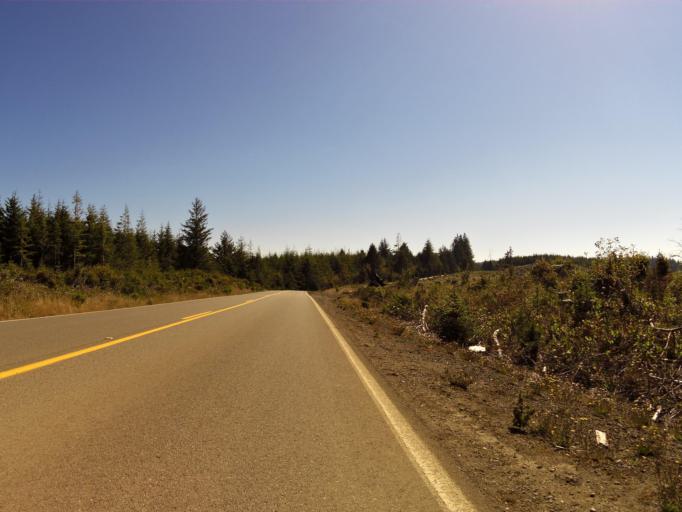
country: US
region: Oregon
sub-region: Coos County
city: Barview
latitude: 43.2568
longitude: -124.3375
